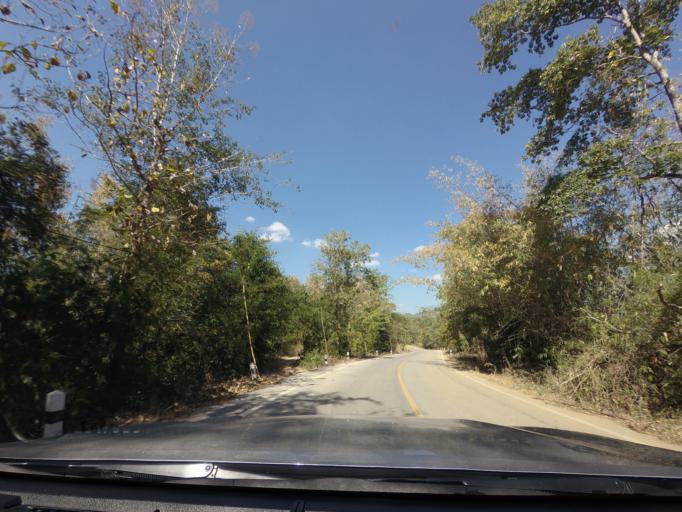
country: TH
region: Lampang
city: Chae Hom
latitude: 18.5332
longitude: 99.6424
